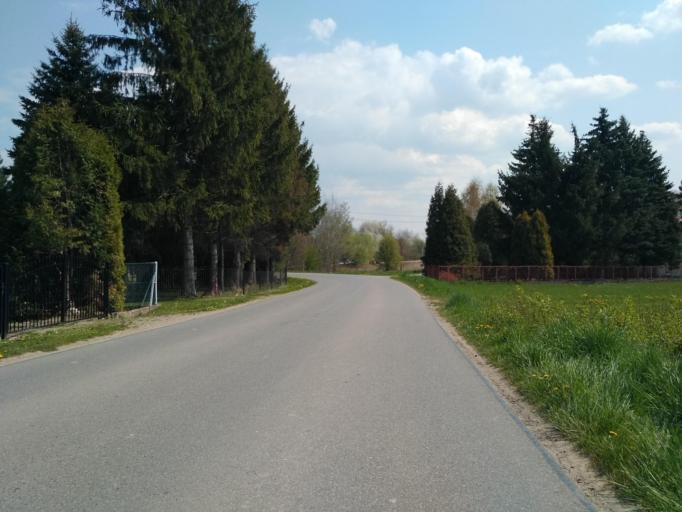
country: PL
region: Subcarpathian Voivodeship
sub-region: Powiat jasielski
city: Tarnowiec
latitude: 49.7455
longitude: 21.5561
